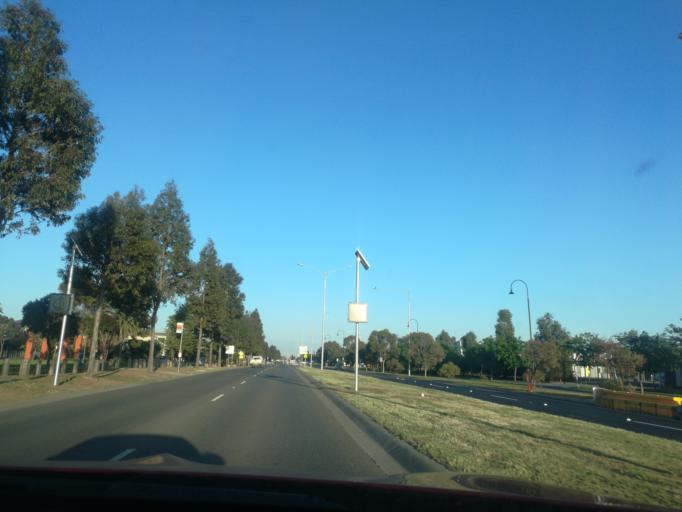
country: AU
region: Victoria
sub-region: Wyndham
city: Williams Landing
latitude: -37.8860
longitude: 144.7454
